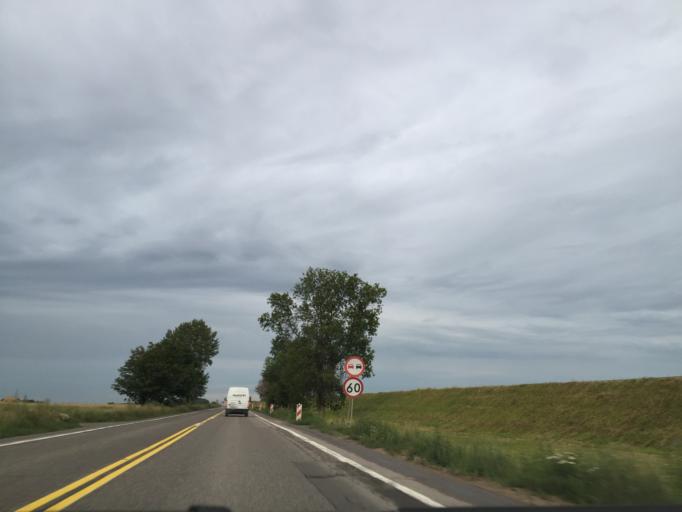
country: PL
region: Podlasie
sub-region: Powiat zambrowski
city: Rutki-Kossaki
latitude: 53.1031
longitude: 22.5461
